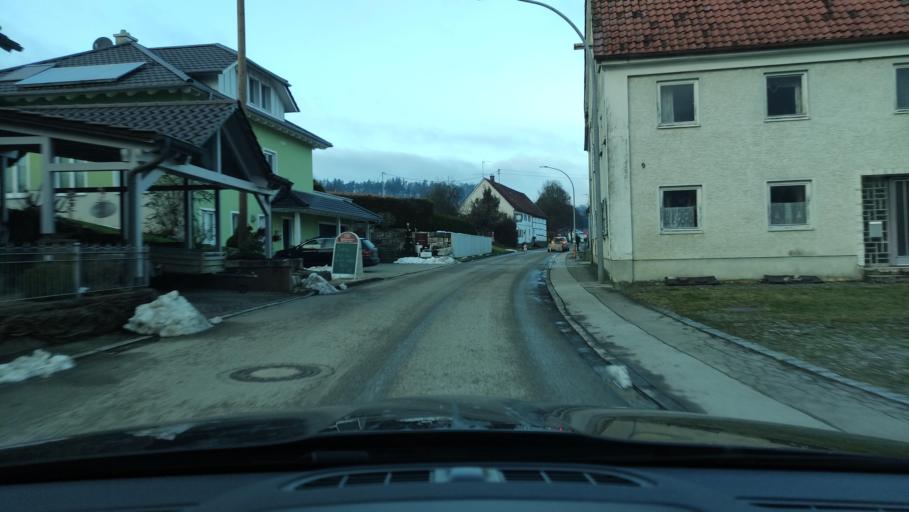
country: DE
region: Bavaria
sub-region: Swabia
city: Deisenhausen
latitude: 48.2951
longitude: 10.3562
